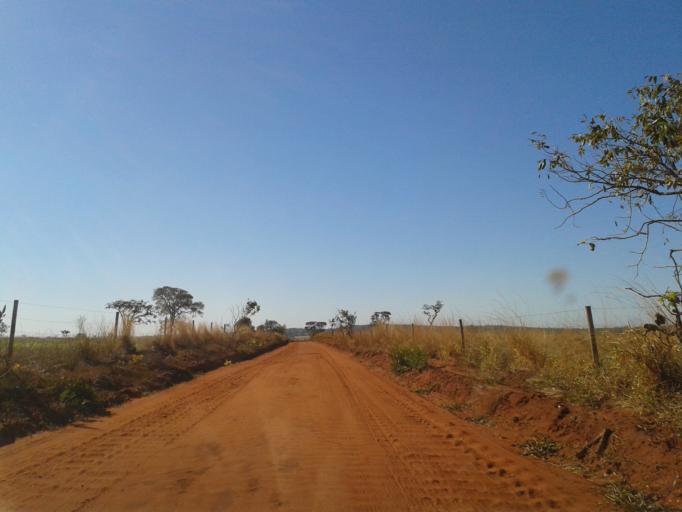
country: BR
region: Minas Gerais
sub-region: Ituiutaba
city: Ituiutaba
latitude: -19.0704
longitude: -49.3386
